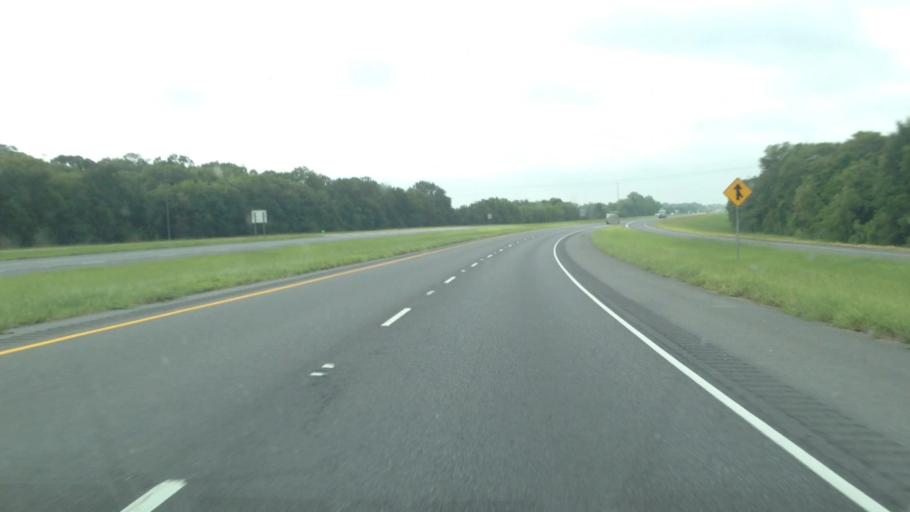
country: US
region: Louisiana
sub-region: Saint Landry Parish
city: Opelousas
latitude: 30.6400
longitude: -92.0490
